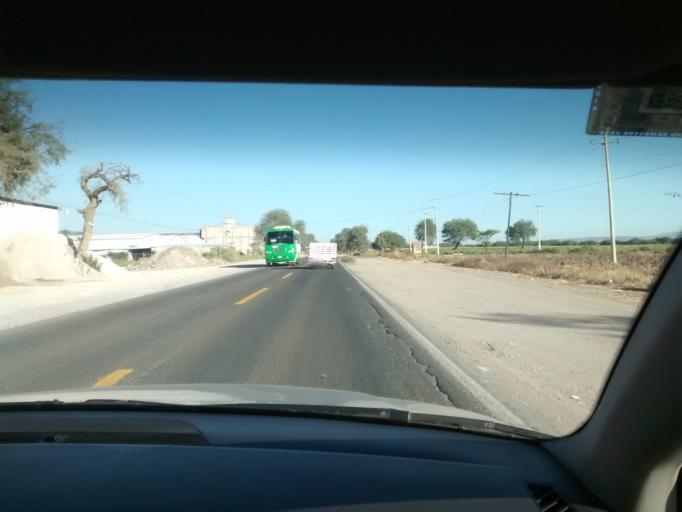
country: MX
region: Puebla
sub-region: Santiago Miahuatlan
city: San Jose Monte Chiquito
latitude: 18.5025
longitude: -97.4795
